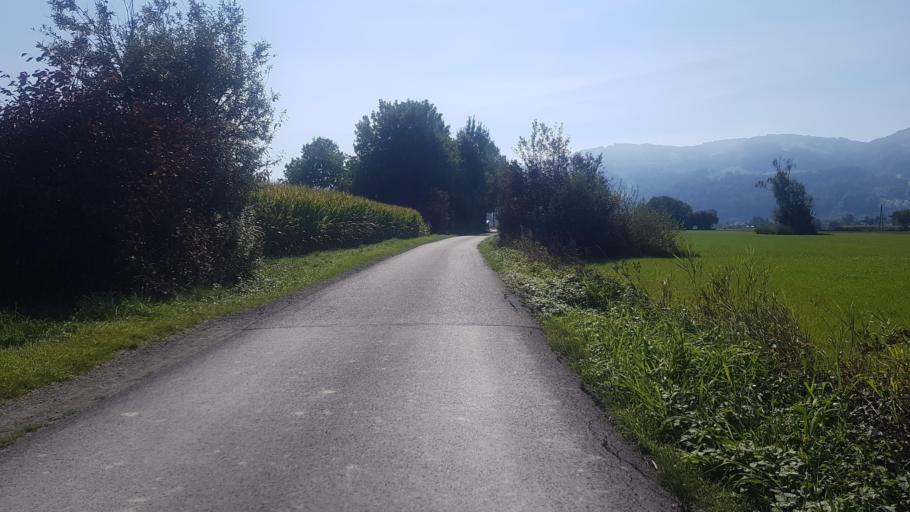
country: AT
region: Vorarlberg
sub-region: Politischer Bezirk Bregenz
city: Gaissau
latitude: 47.4803
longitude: 9.5971
